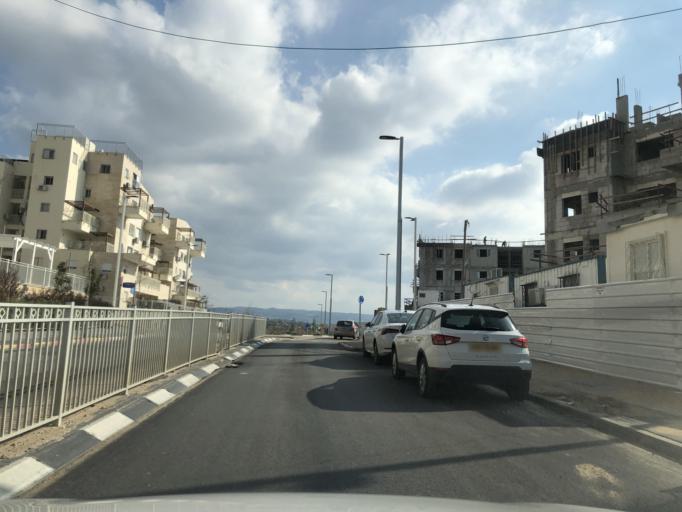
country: IL
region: Jerusalem
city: Modiin Ilit
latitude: 31.9340
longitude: 35.0526
